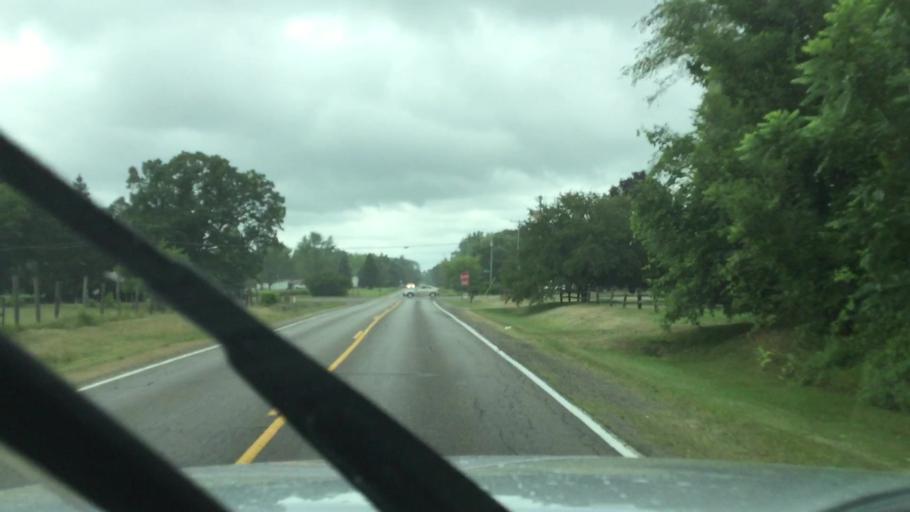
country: US
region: Michigan
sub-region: Genesee County
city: Clio
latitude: 43.1472
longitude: -83.7740
